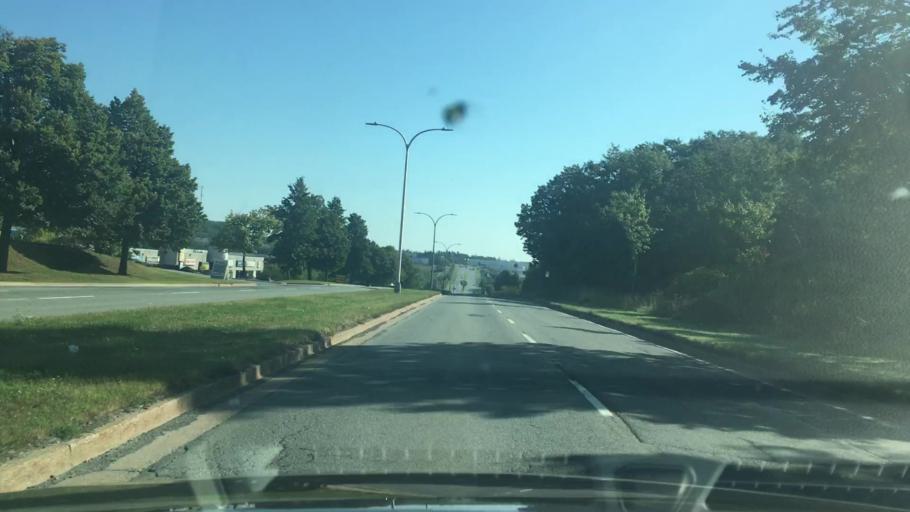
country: CA
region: Nova Scotia
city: Dartmouth
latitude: 44.7130
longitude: -63.5956
